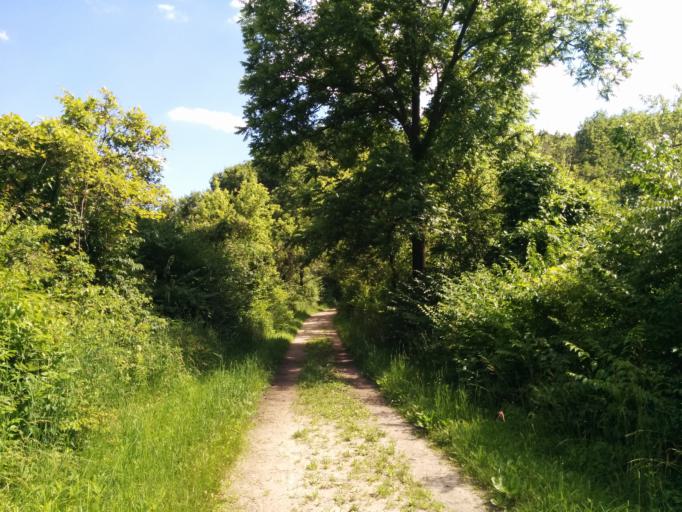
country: US
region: Illinois
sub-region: Will County
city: Goodings Grove
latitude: 41.6788
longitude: -87.8987
